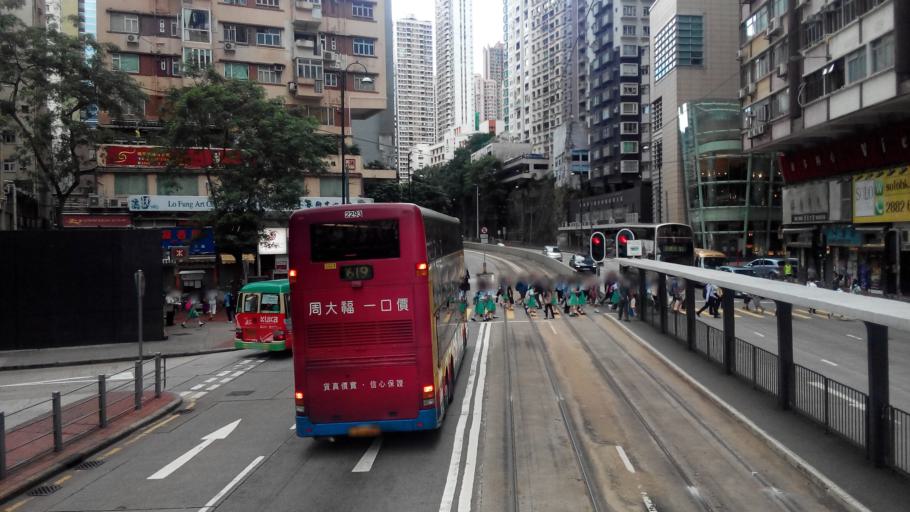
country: HK
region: Wanchai
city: Wan Chai
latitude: 22.2828
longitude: 114.1922
